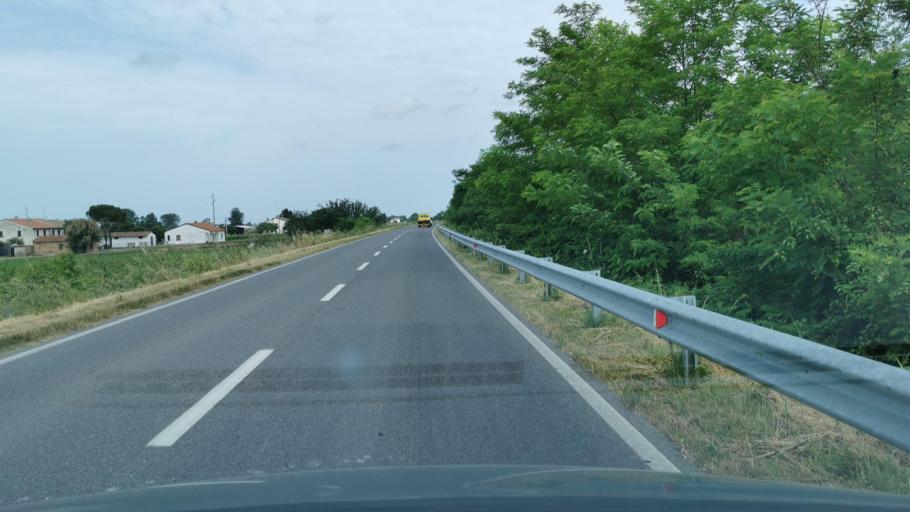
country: IT
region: Emilia-Romagna
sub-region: Provincia di Ravenna
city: Sant'Alberto
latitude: 44.5379
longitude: 12.1837
